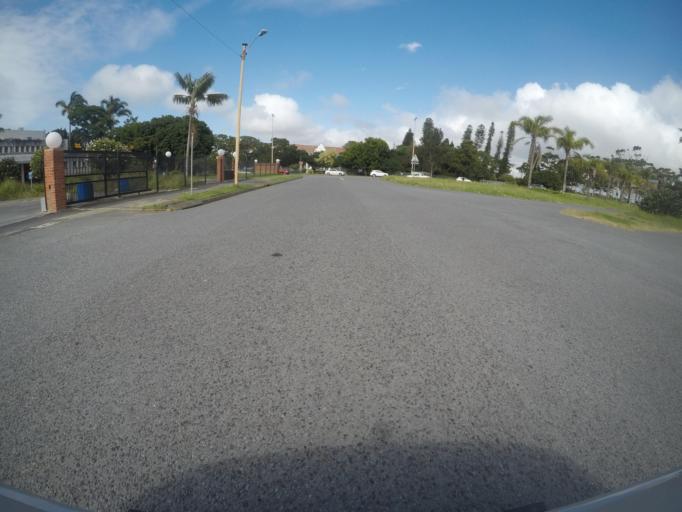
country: ZA
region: Eastern Cape
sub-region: Buffalo City Metropolitan Municipality
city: East London
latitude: -32.9941
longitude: 27.8972
